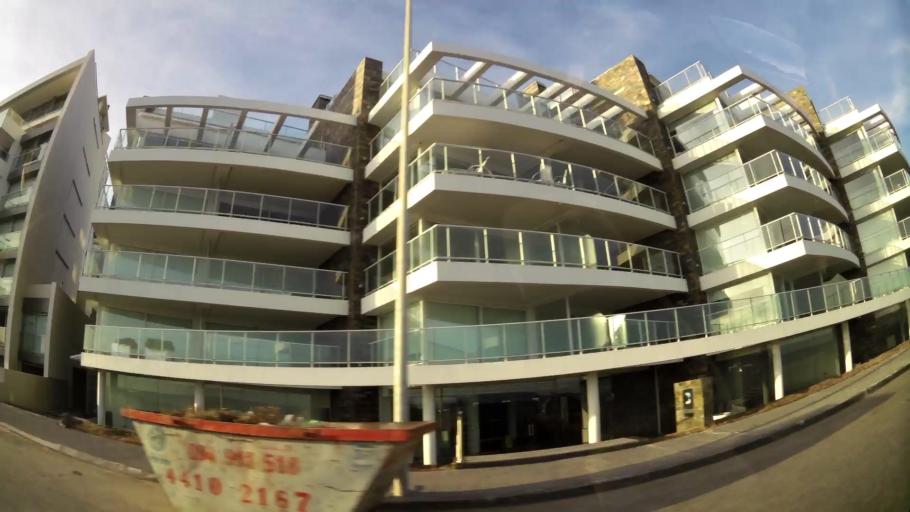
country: UY
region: Maldonado
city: Punta del Este
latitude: -34.9670
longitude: -54.9460
